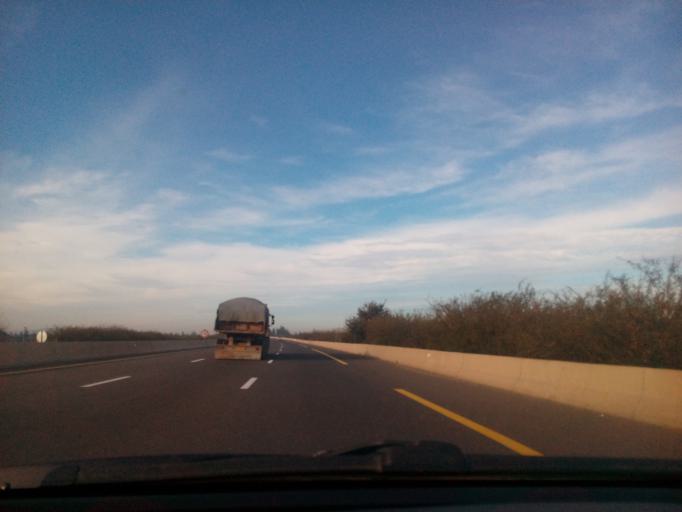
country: DZ
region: Mascara
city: Sig
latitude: 35.6161
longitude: 0.0024
